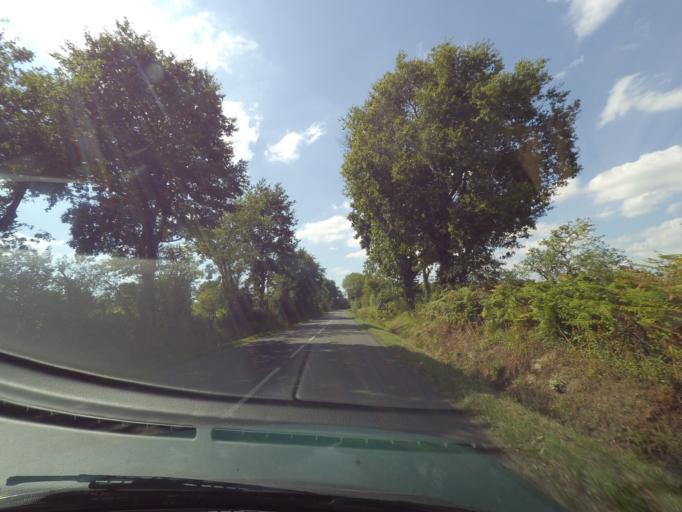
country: FR
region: Pays de la Loire
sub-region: Departement de la Loire-Atlantique
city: Sainte-Pazanne
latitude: 47.0790
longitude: -1.8024
